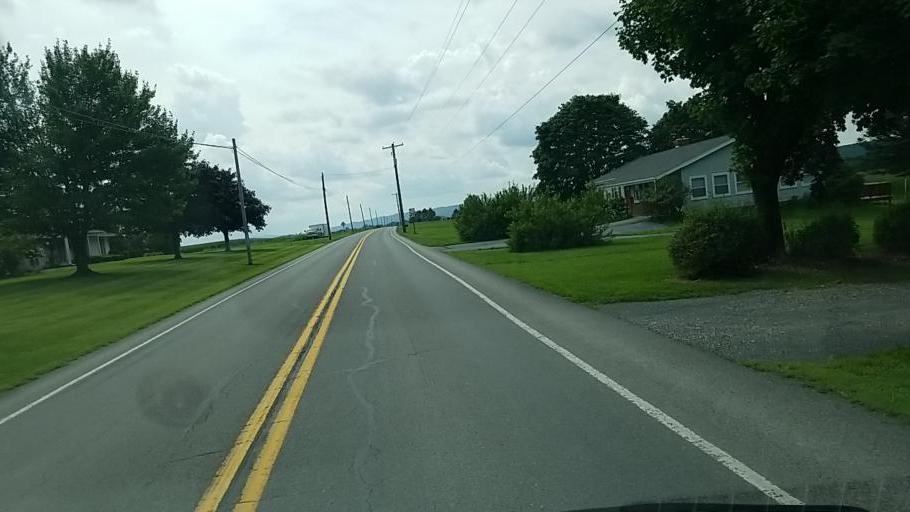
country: US
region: Pennsylvania
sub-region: Dauphin County
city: Elizabethville
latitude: 40.6065
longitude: -76.7786
